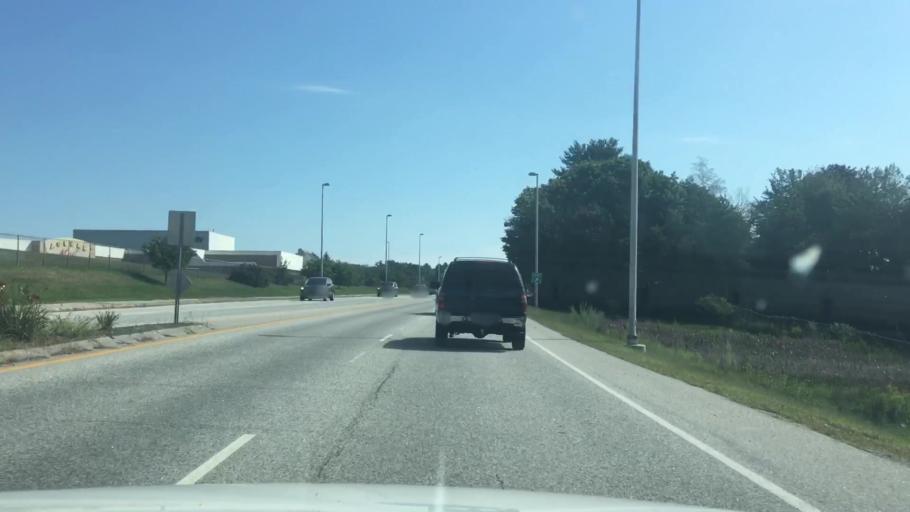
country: US
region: Maine
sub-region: Androscoggin County
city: Auburn
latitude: 44.1207
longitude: -70.2303
